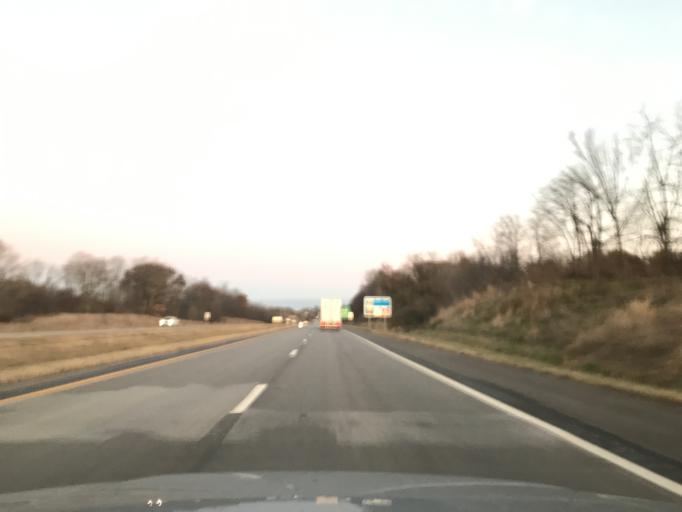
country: US
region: Missouri
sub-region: Marion County
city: Hannibal
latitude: 39.7143
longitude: -91.4089
